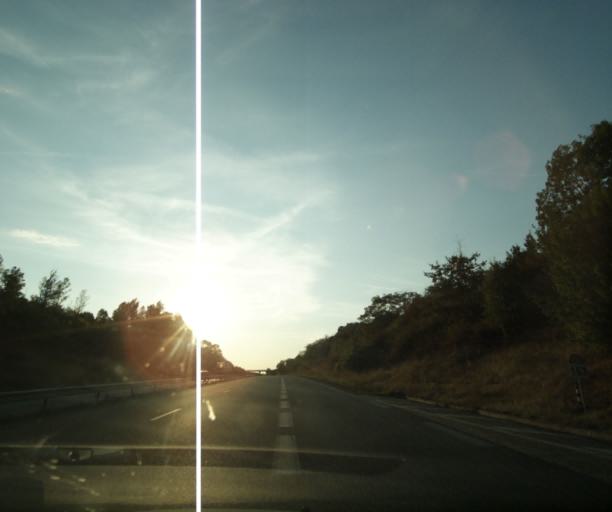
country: FR
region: Midi-Pyrenees
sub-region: Departement du Tarn-et-Garonne
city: Auvillar
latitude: 44.0596
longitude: 0.9087
